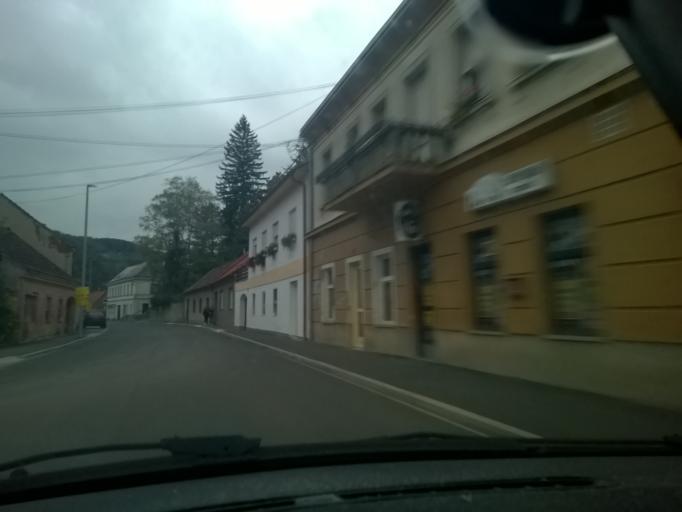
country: HR
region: Krapinsko-Zagorska
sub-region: Grad Krapina
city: Krapina
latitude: 46.1669
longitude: 15.8671
